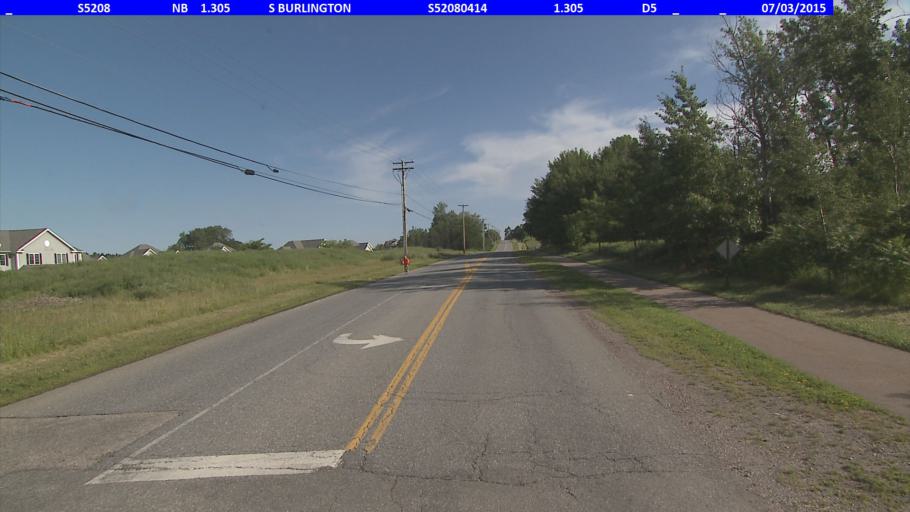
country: US
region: Vermont
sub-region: Chittenden County
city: South Burlington
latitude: 44.4295
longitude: -73.1749
